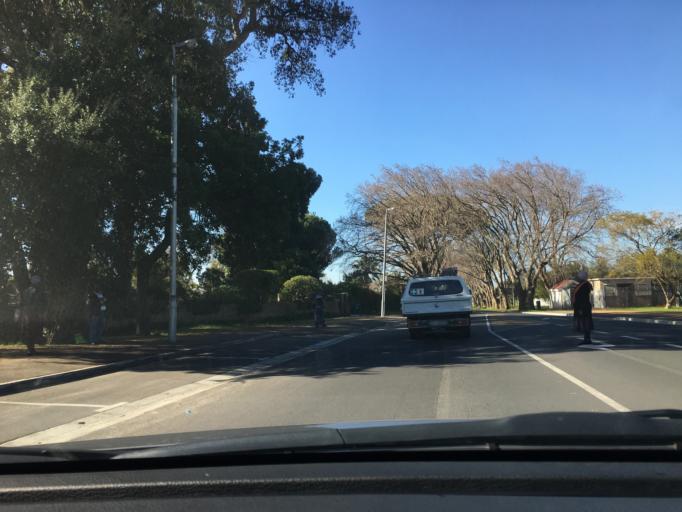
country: ZA
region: Western Cape
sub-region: City of Cape Town
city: Constantia
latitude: -34.0215
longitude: 18.4387
